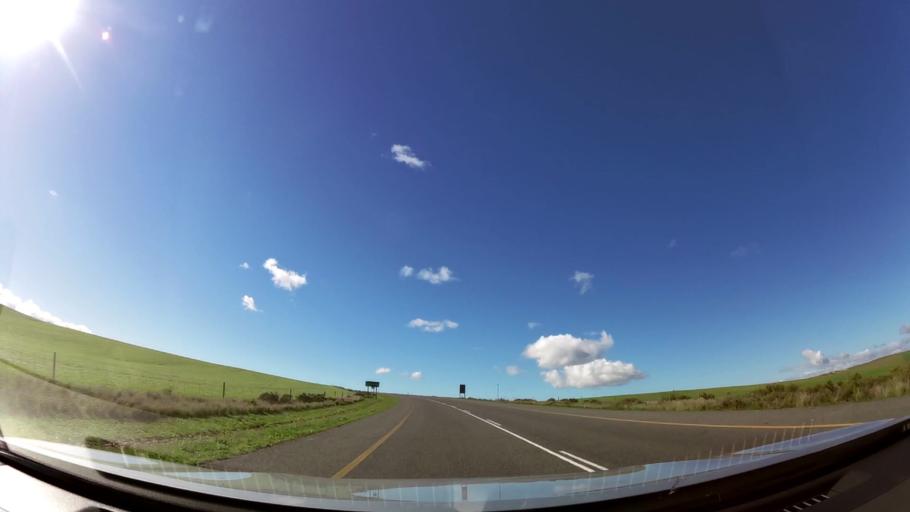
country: ZA
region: Western Cape
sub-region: Overberg District Municipality
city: Caledon
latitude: -34.1857
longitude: 19.7017
